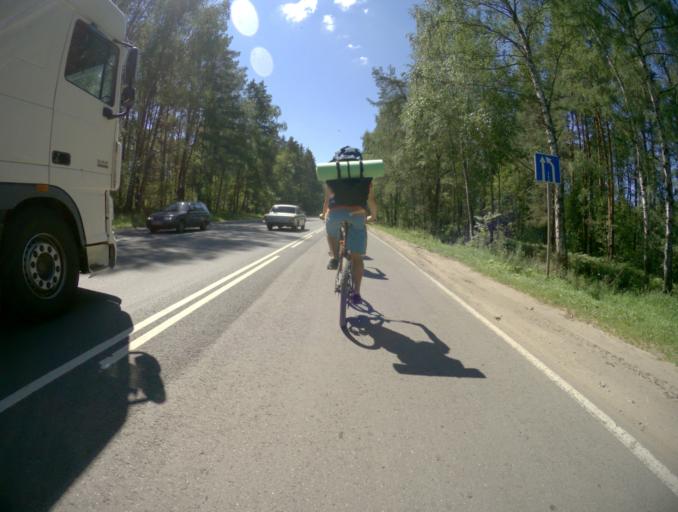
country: RU
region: Nizjnij Novgorod
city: Neklyudovo
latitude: 56.4414
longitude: 44.0023
